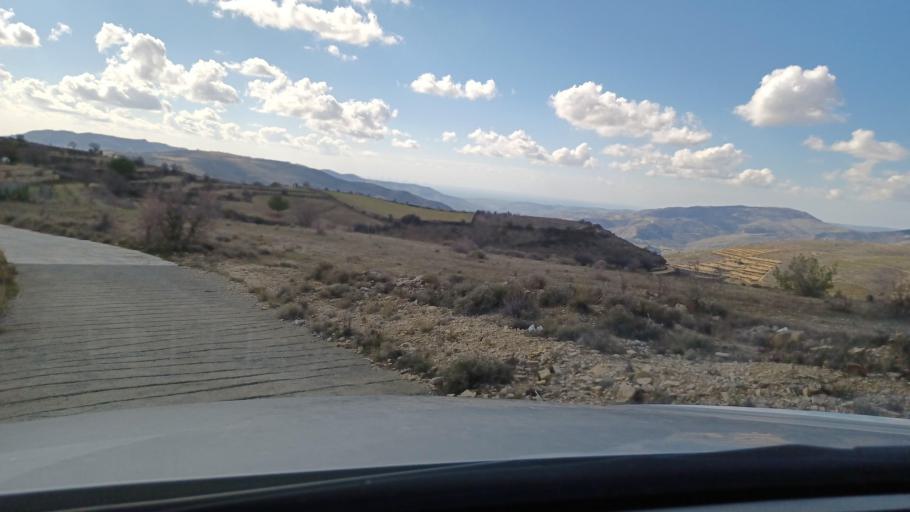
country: CY
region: Limassol
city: Pachna
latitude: 34.8229
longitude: 32.7652
